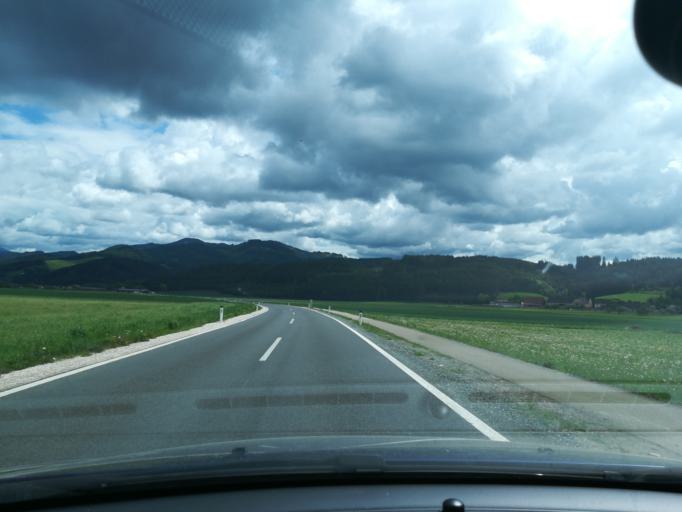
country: AT
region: Styria
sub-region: Politischer Bezirk Murtal
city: Grosslobming
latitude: 47.1813
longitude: 14.7795
